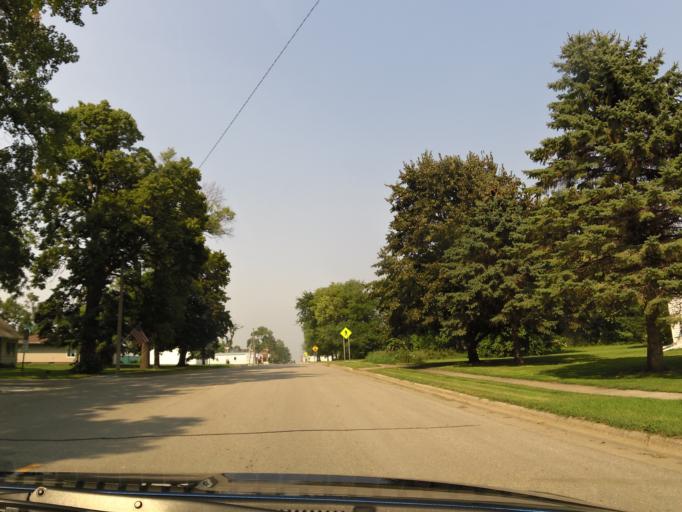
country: US
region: Minnesota
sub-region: Grant County
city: Elbow Lake
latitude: 46.0335
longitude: -96.1007
